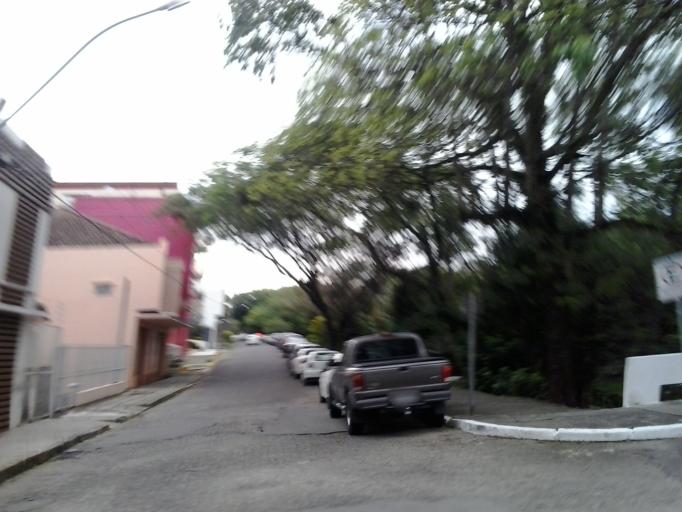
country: BR
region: Rio Grande do Sul
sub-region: Santa Maria
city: Santa Maria
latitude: -29.6866
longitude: -53.8027
